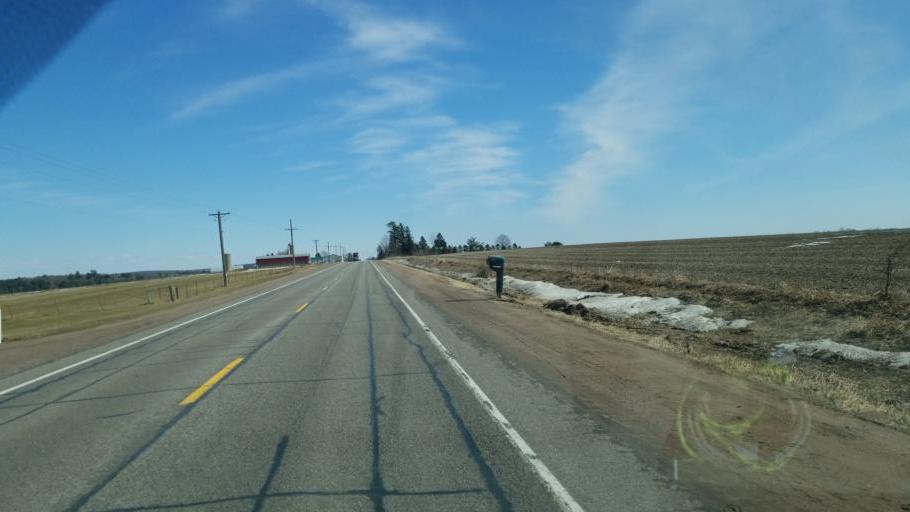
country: US
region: Wisconsin
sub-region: Clark County
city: Loyal
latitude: 44.5821
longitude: -90.4254
